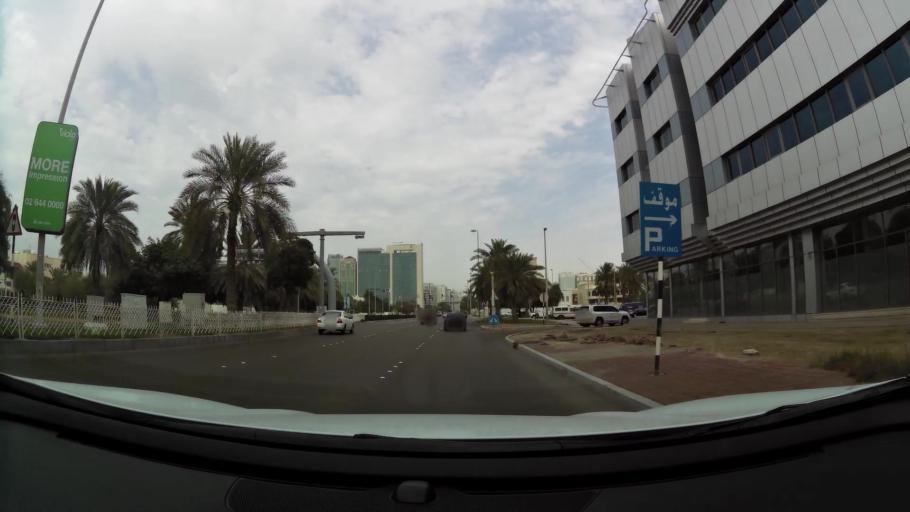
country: AE
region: Abu Dhabi
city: Abu Dhabi
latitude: 24.4638
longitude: 54.3638
